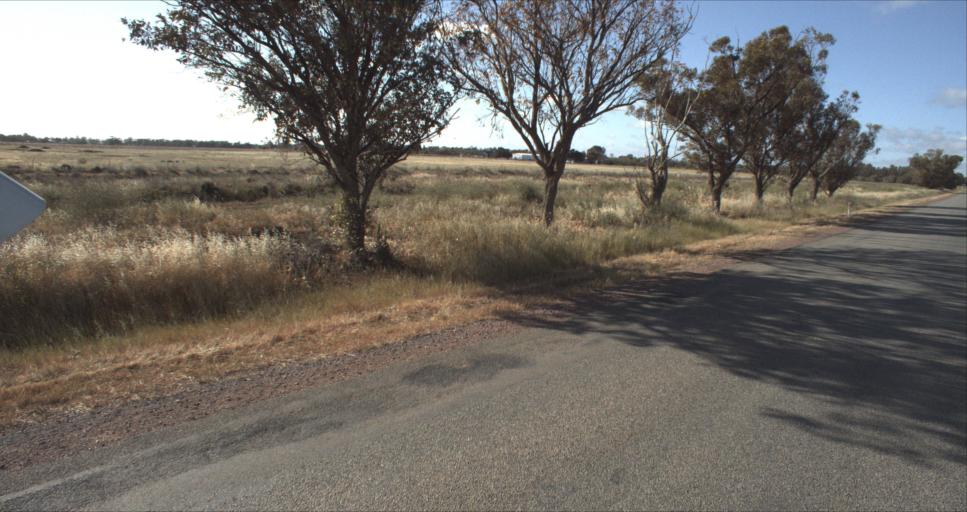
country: AU
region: New South Wales
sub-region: Leeton
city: Leeton
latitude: -34.5214
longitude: 146.3905
